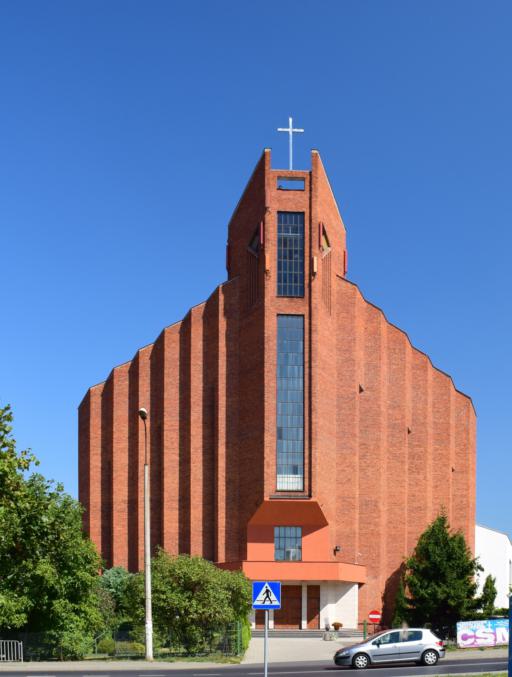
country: PL
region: Lublin Voivodeship
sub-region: Powiat lubelski
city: Lublin
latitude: 51.2531
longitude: 22.5223
